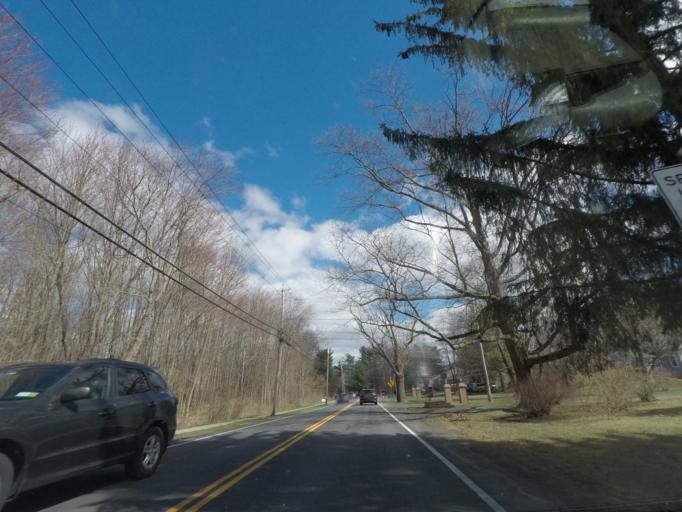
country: US
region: New York
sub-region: Albany County
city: Delmar
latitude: 42.6024
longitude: -73.8059
